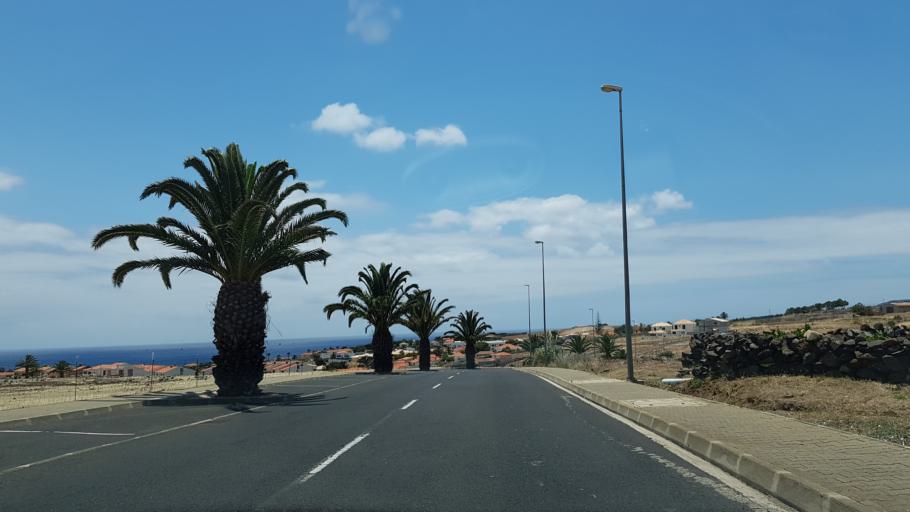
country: PT
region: Madeira
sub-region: Porto Santo
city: Vila de Porto Santo
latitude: 33.0644
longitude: -16.3436
